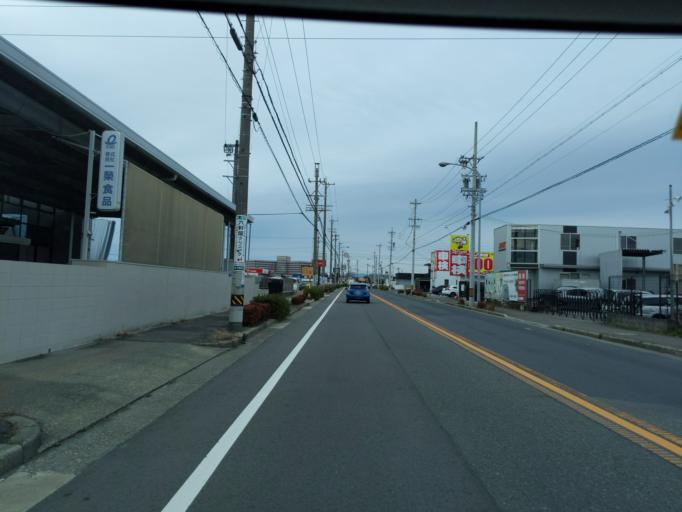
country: JP
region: Aichi
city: Kasugai
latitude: 35.2633
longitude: 136.9728
